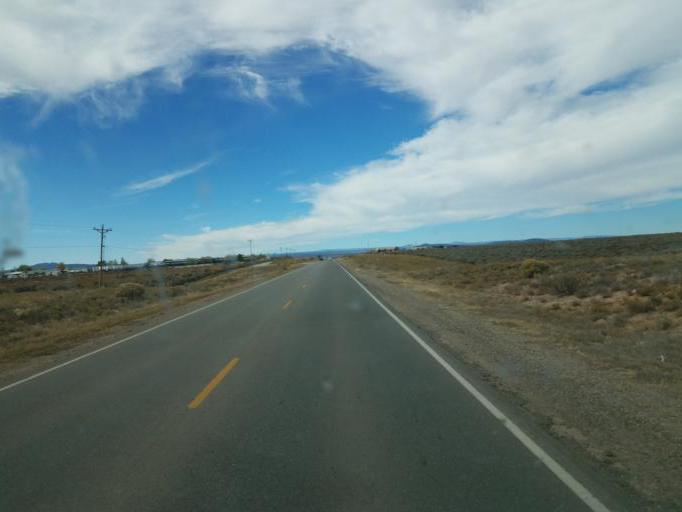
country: US
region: New Mexico
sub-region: Taos County
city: Taos
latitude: 36.4597
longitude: -105.6323
